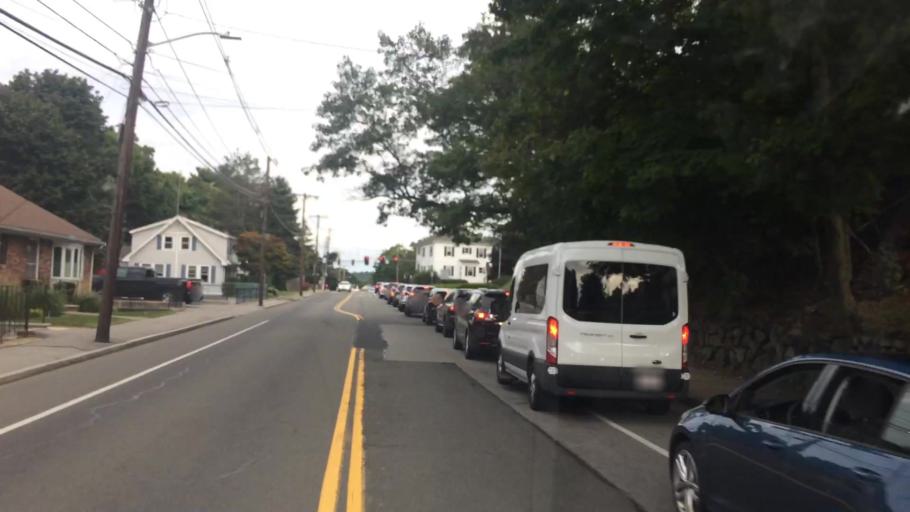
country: US
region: Massachusetts
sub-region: Middlesex County
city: Woburn
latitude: 42.4858
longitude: -71.1618
